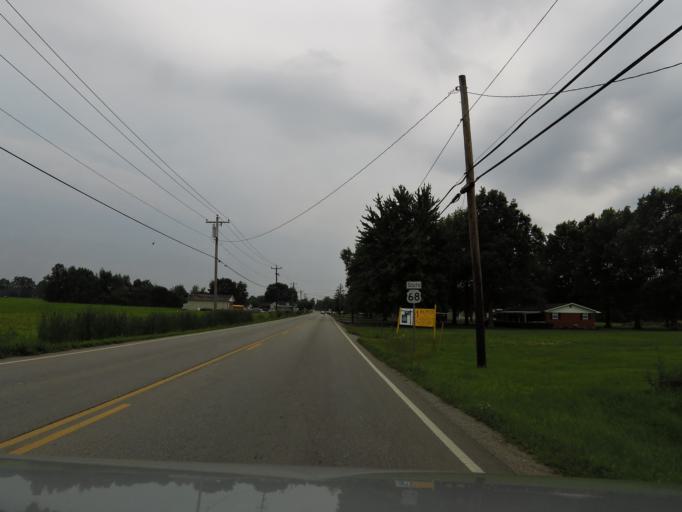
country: US
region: Ohio
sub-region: Brown County
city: Georgetown
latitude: 38.9135
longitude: -83.9031
